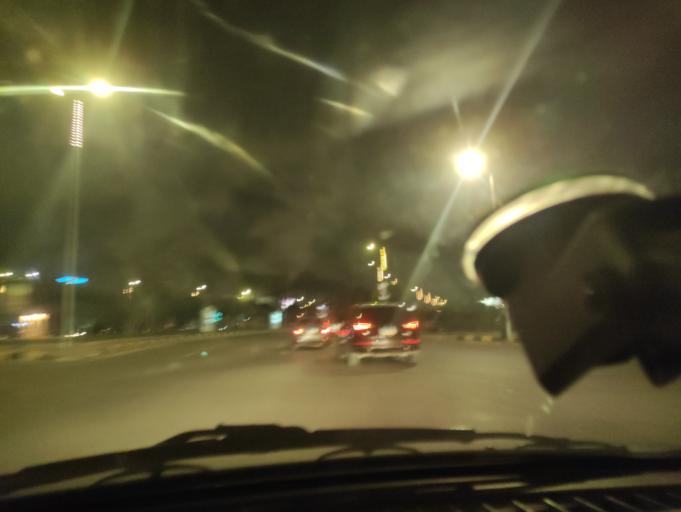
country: EG
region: Al Jizah
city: Awsim
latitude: 30.0219
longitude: 31.0048
